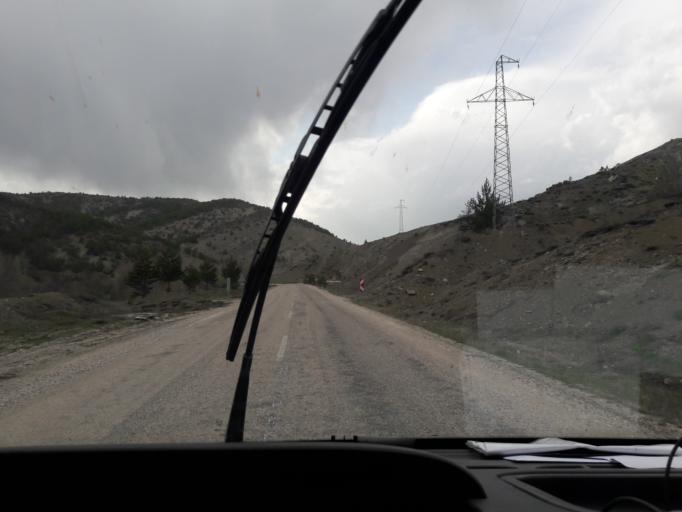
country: TR
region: Giresun
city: Alucra
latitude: 40.2805
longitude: 38.8229
